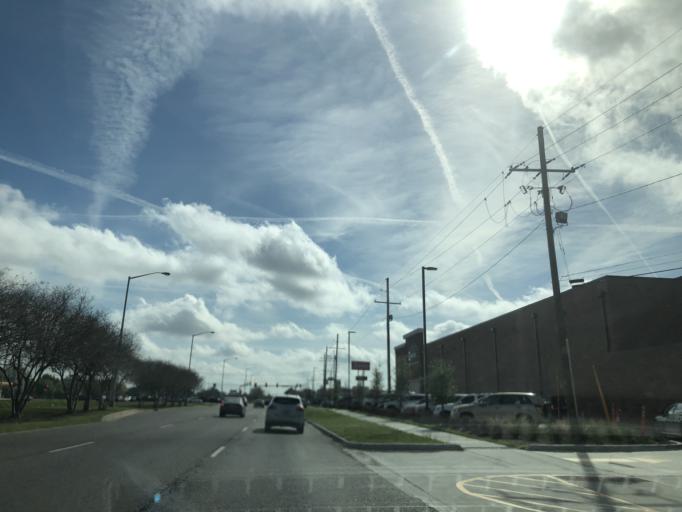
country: US
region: Louisiana
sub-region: Jefferson Parish
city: Metairie Terrace
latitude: 30.0057
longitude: -90.1971
